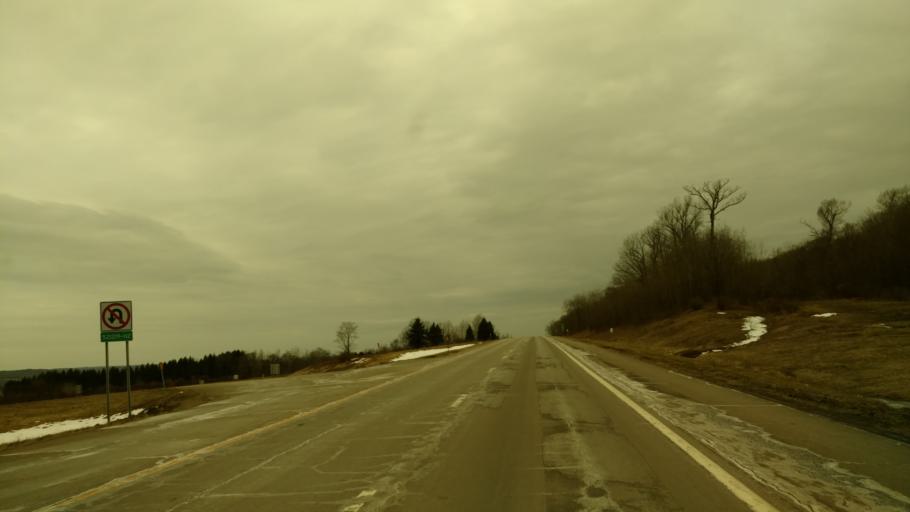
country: US
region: New York
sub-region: Chautauqua County
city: Lakewood
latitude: 42.1412
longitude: -79.3531
